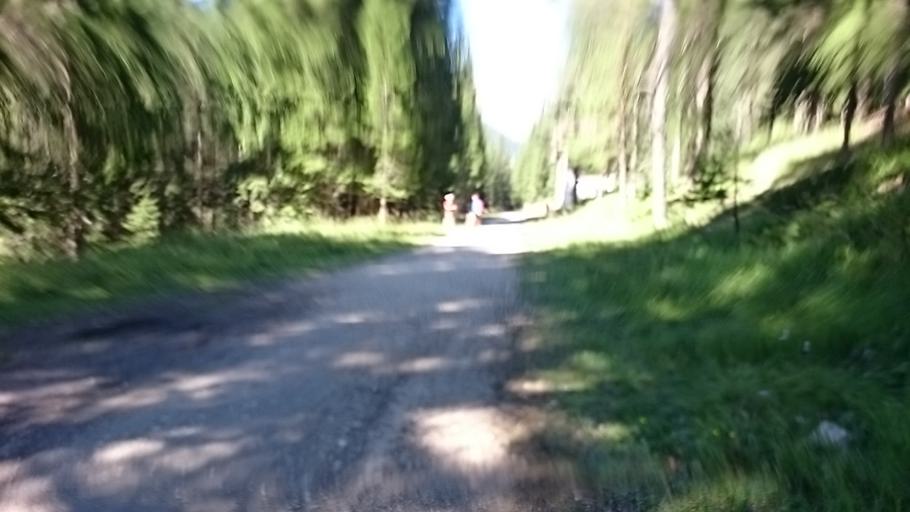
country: IT
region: Veneto
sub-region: Provincia di Belluno
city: Cortina d'Ampezzo
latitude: 46.6016
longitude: 12.1383
